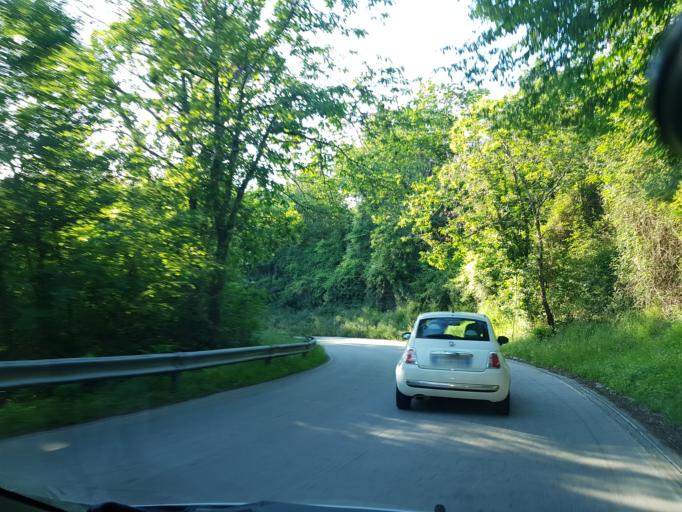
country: IT
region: Tuscany
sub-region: Provincia di Massa-Carrara
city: Casola in Lunigiana
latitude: 44.1867
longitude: 10.1935
